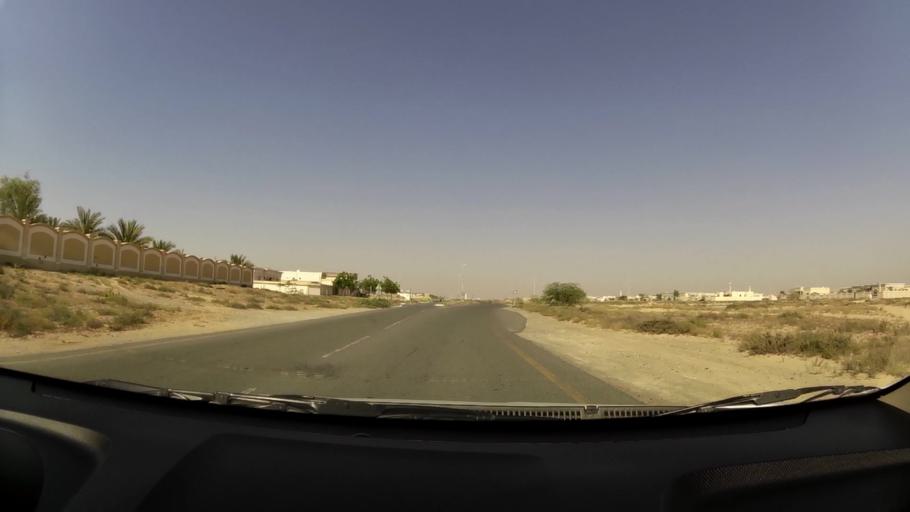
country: AE
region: Umm al Qaywayn
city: Umm al Qaywayn
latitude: 25.4873
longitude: 55.5817
